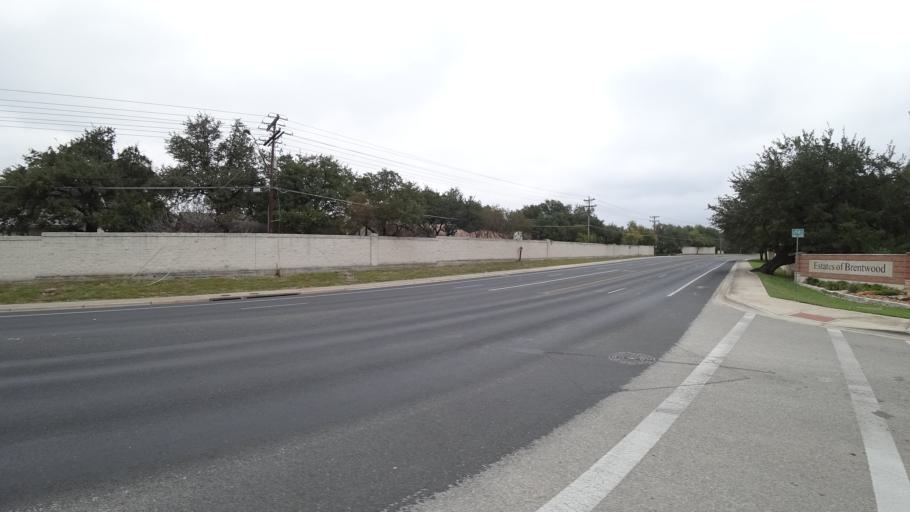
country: US
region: Texas
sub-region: Williamson County
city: Anderson Mill
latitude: 30.4501
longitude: -97.8192
